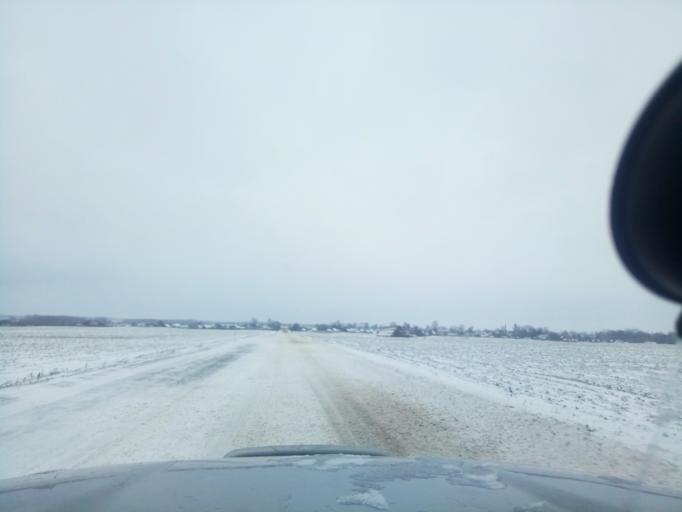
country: BY
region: Minsk
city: Tsimkavichy
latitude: 53.0609
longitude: 26.9653
